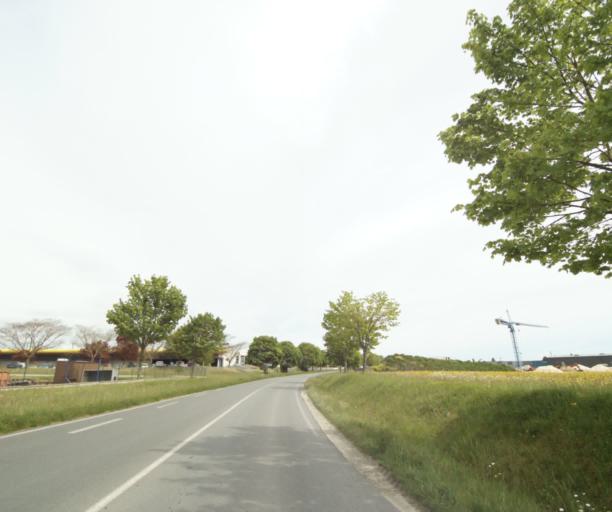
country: FR
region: Poitou-Charentes
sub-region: Departement de la Charente-Maritime
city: Les Gonds
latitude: 45.7165
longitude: -0.6513
